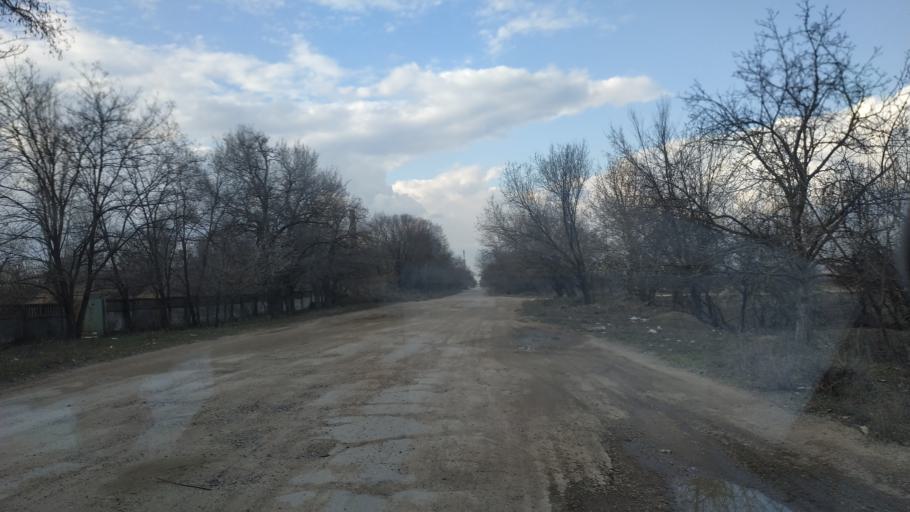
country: MD
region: Anenii Noi
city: Varnita
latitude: 46.8935
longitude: 29.4624
